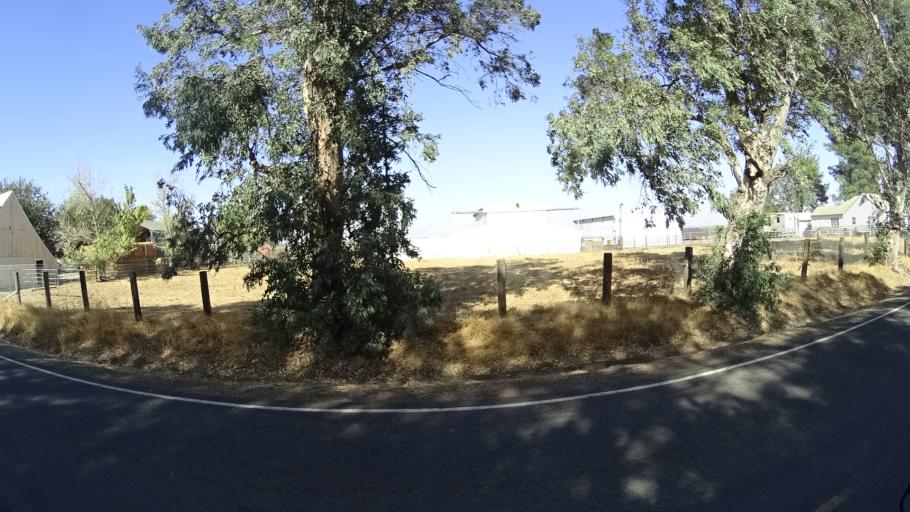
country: US
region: California
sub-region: Yolo County
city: Winters
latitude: 38.5906
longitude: -121.8642
